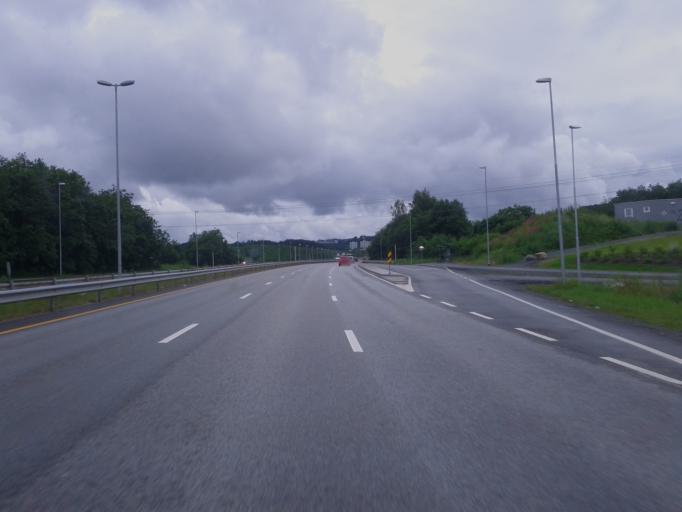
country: NO
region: Sor-Trondelag
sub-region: Trondheim
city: Trondheim
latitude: 63.3960
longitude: 10.3910
